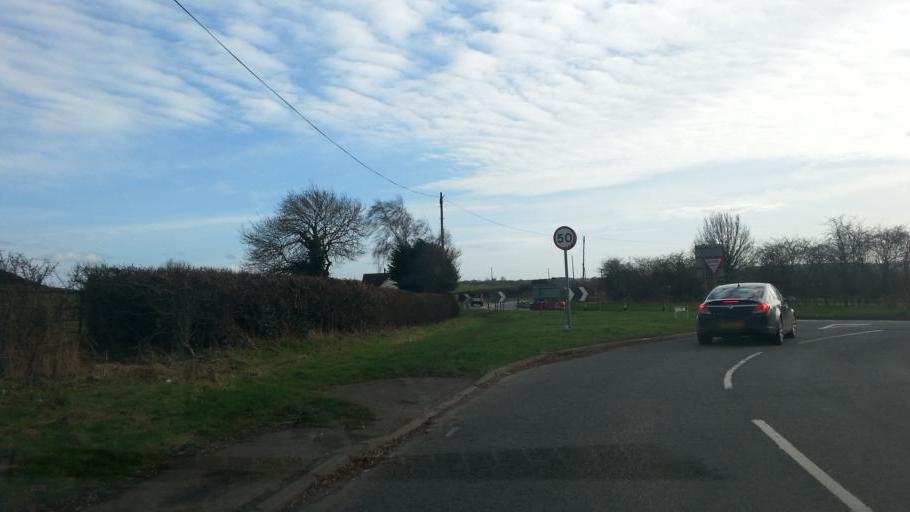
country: GB
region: England
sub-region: Staffordshire
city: Colwich
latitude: 52.8163
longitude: -2.0012
